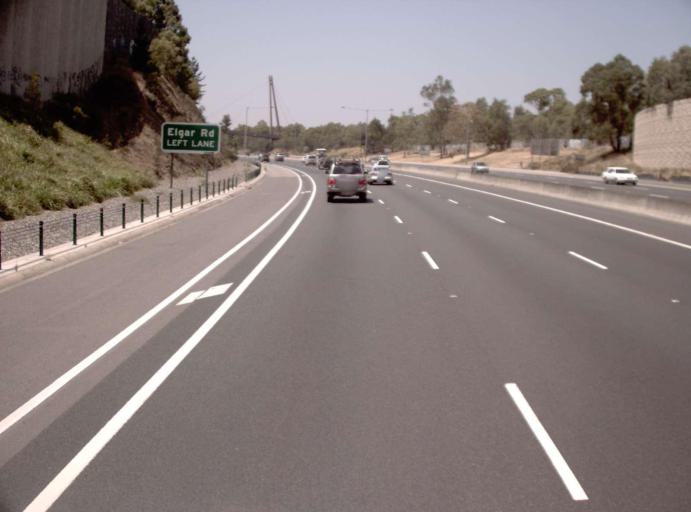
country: AU
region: Victoria
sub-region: Whitehorse
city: Mont Albert North
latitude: -37.7934
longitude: 145.1091
